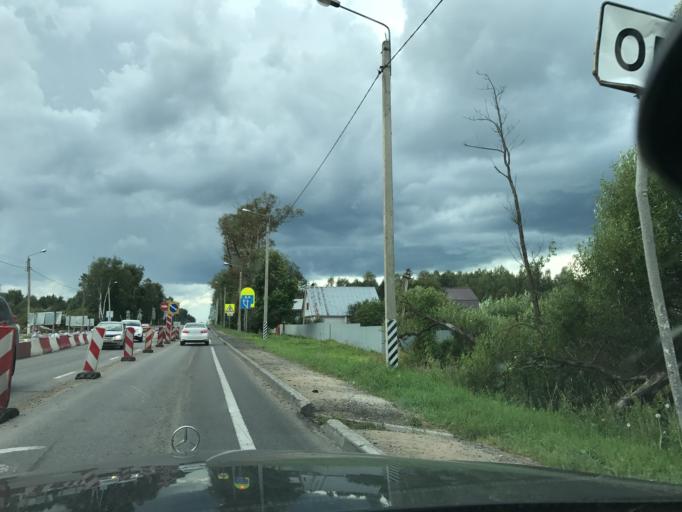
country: RU
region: Vladimir
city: Petushki
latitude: 55.9282
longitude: 39.3221
